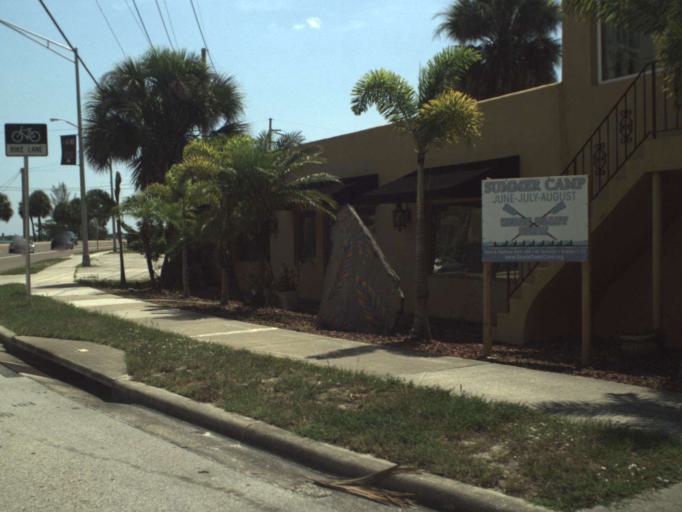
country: US
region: Florida
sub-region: Brevard County
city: Indian Harbour Beach
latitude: 28.1302
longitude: -80.6256
